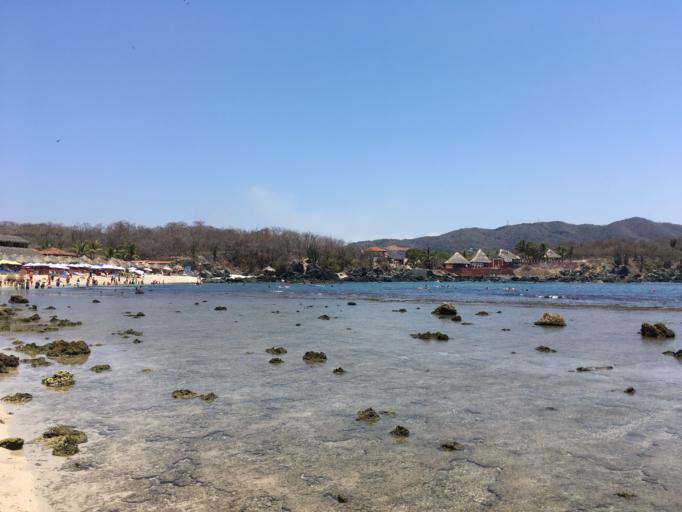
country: MX
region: Guerrero
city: Ixtapa
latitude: 17.6764
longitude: -101.6566
